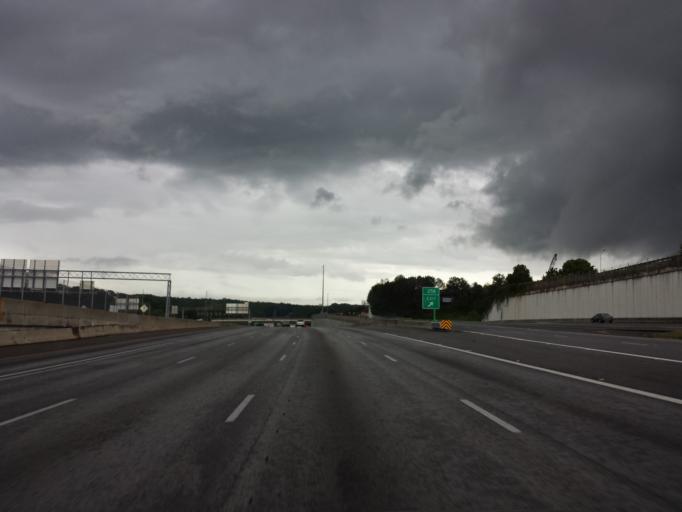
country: US
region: Georgia
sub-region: Cobb County
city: Vinings
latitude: 33.8851
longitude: -84.4572
